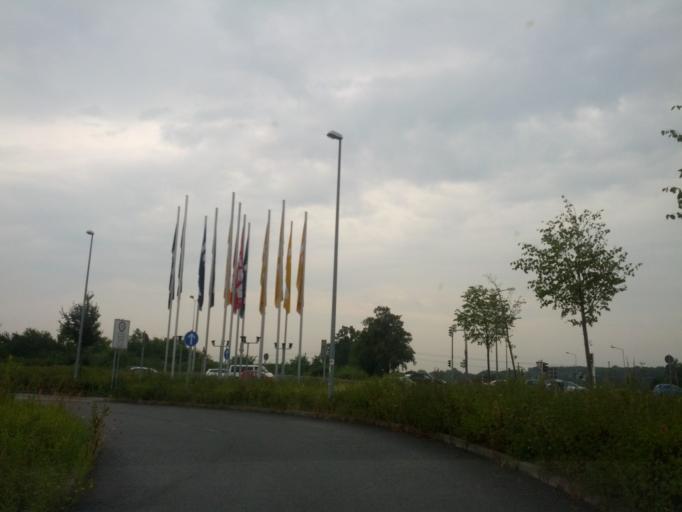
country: DE
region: Mecklenburg-Vorpommern
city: Lambrechtshagen
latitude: 54.1071
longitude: 12.0498
